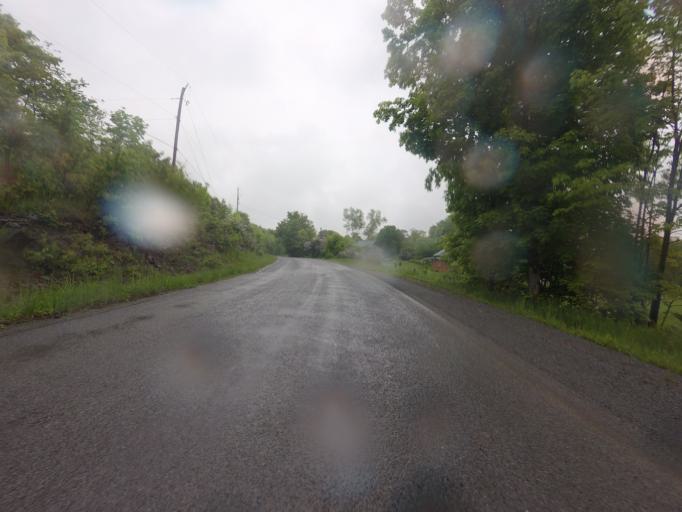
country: CA
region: Ontario
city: Kingston
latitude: 44.4852
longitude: -76.4524
